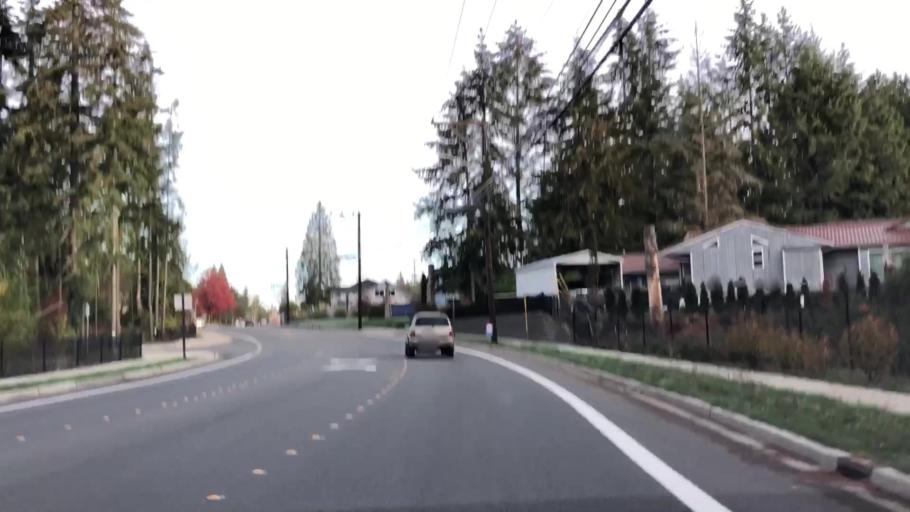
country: US
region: Washington
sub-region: Snohomish County
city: Martha Lake
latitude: 47.8431
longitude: -122.2357
